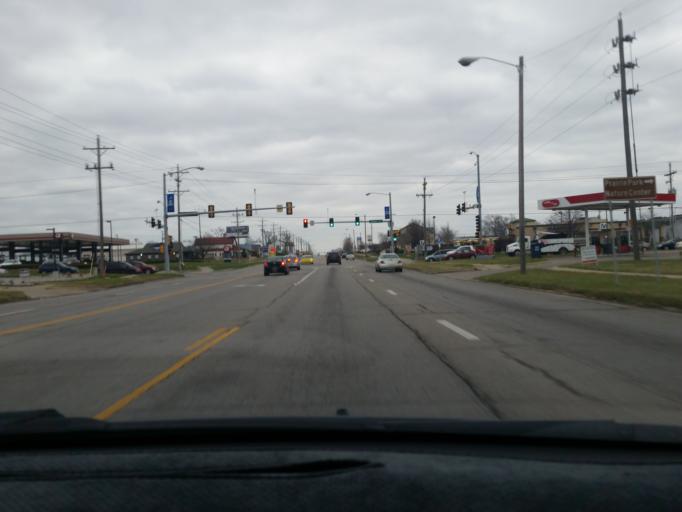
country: US
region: Kansas
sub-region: Douglas County
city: Lawrence
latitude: 38.9427
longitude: -95.2244
